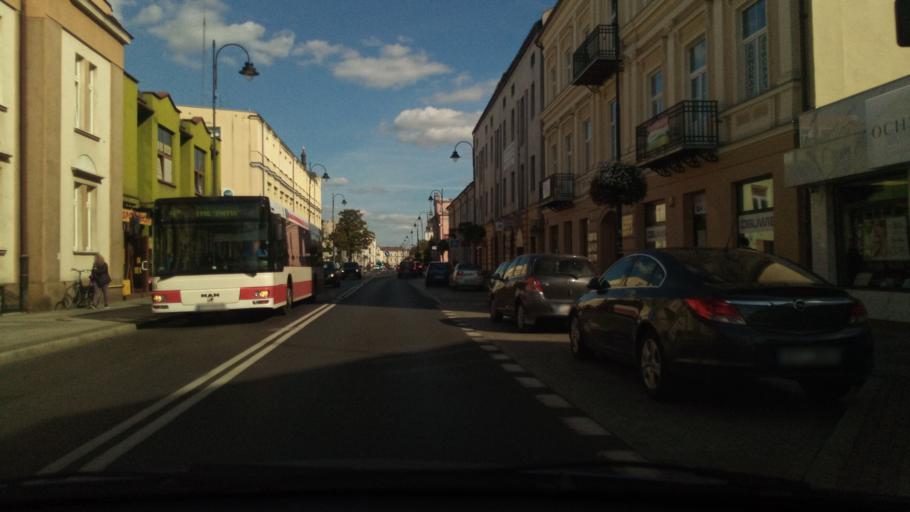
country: PL
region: Lodz Voivodeship
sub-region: Piotrkow Trybunalski
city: Piotrkow Trybunalski
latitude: 51.4092
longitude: 19.6872
